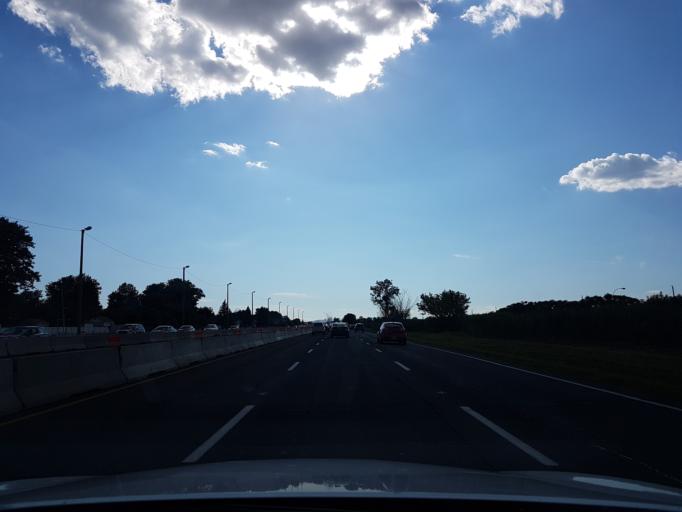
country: CA
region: Quebec
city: Saint-Bruno-de-Montarville
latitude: 45.5091
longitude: -73.4145
